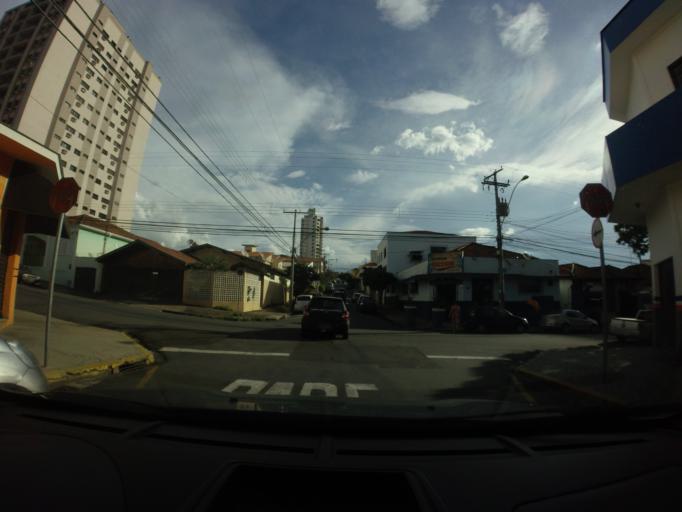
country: BR
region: Sao Paulo
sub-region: Piracicaba
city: Piracicaba
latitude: -22.7259
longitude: -47.6406
